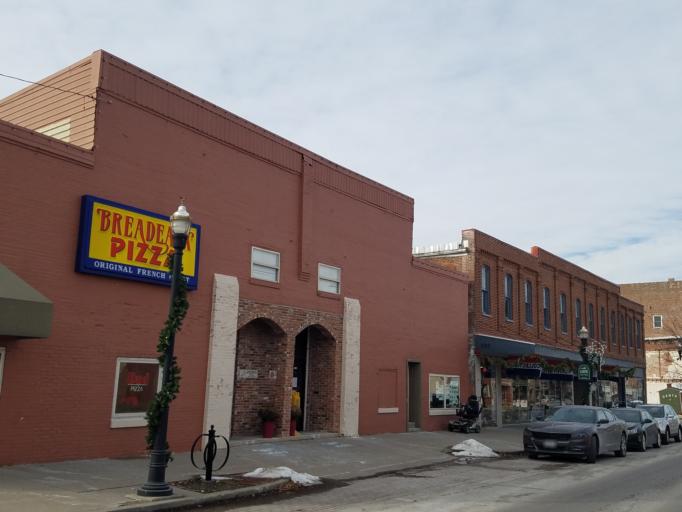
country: US
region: Missouri
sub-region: Cooper County
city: Boonville
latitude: 38.9738
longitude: -92.7435
